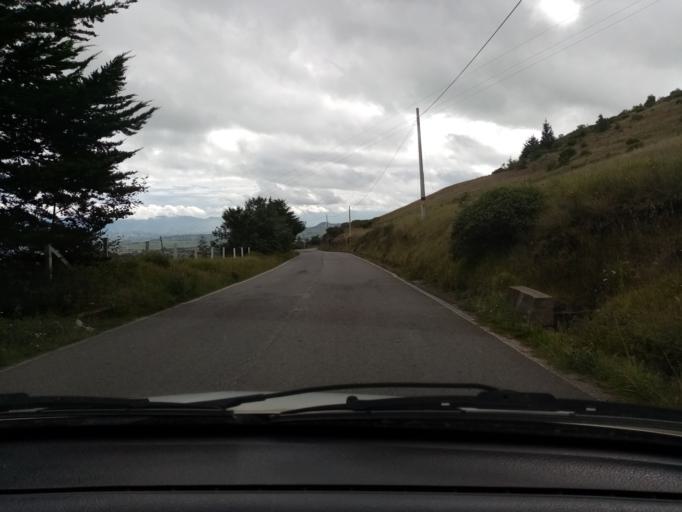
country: CO
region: Boyaca
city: Siachoque
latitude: 5.5695
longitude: -73.2748
